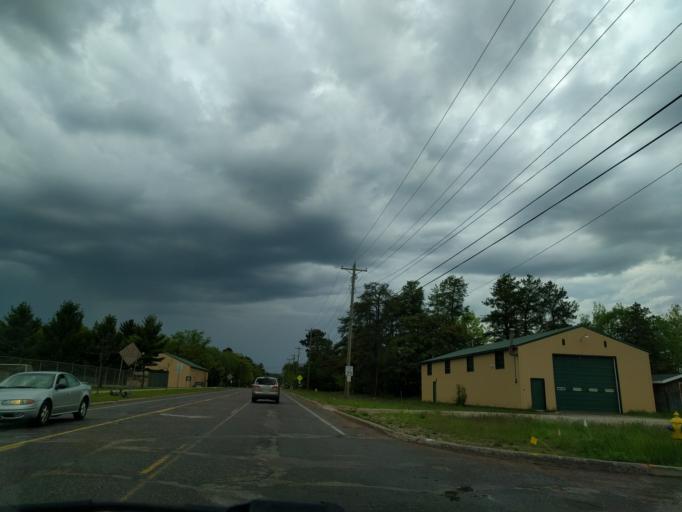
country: US
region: Michigan
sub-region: Marquette County
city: Trowbridge Park
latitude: 46.5640
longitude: -87.4138
